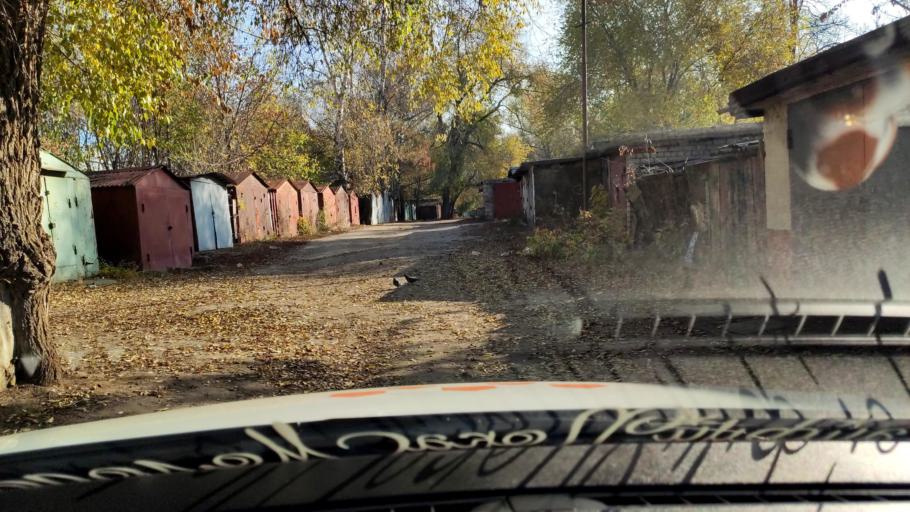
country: RU
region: Voronezj
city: Voronezh
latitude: 51.6764
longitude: 39.1446
